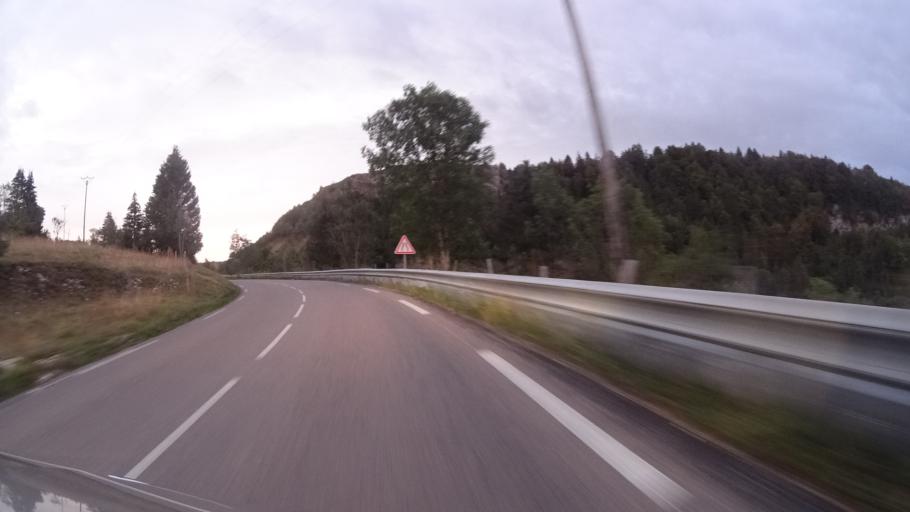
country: CH
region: Vaud
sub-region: Jura-Nord vaudois District
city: Le Chenit
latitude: 46.6718
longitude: 6.1079
